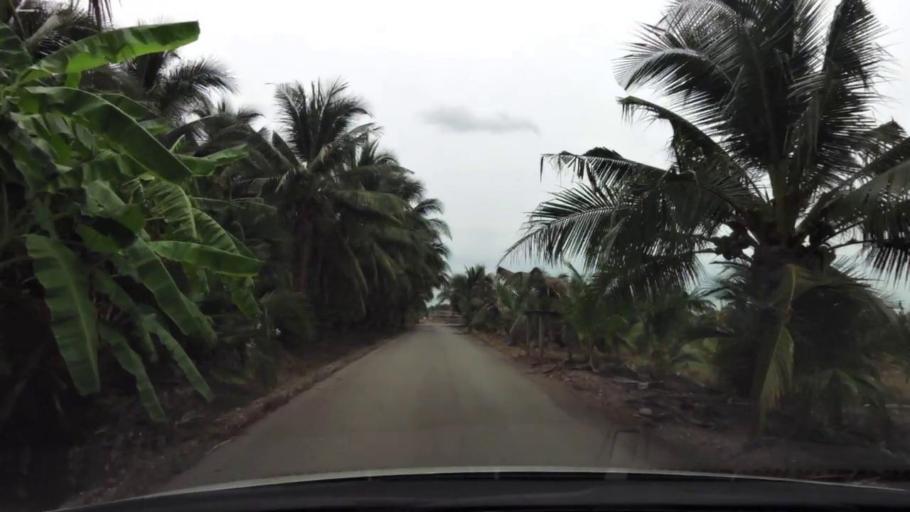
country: TH
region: Samut Sakhon
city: Ban Phaeo
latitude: 13.6015
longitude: 100.0289
